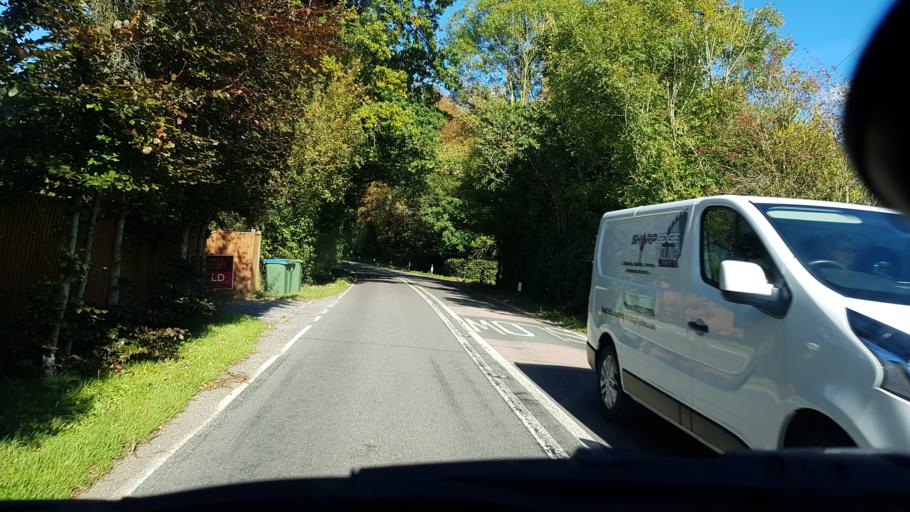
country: GB
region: England
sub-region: West Sussex
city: Billingshurst
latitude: 51.0178
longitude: -0.4350
